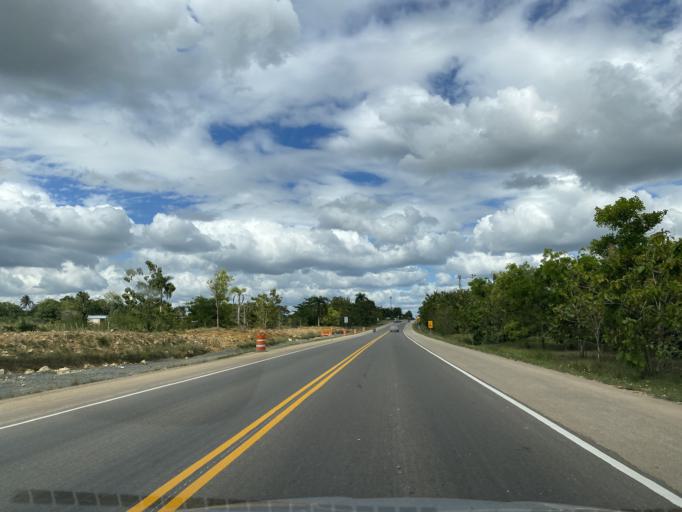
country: DO
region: Santo Domingo
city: Guerra
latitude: 18.5636
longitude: -69.7681
